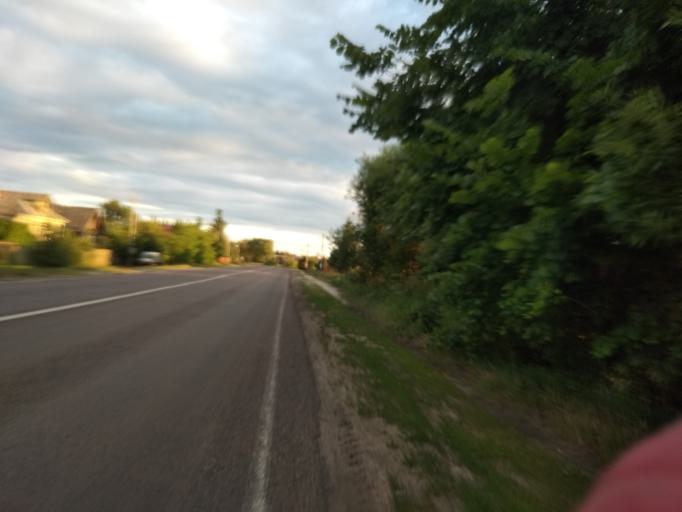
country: RU
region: Moskovskaya
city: Kerva
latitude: 55.5941
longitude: 39.7017
